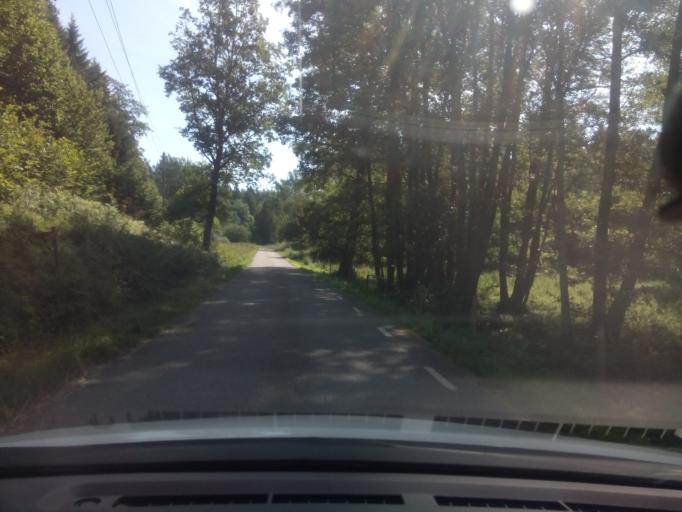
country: SE
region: Soedermanland
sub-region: Trosa Kommun
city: Trosa
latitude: 58.8041
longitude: 17.3662
